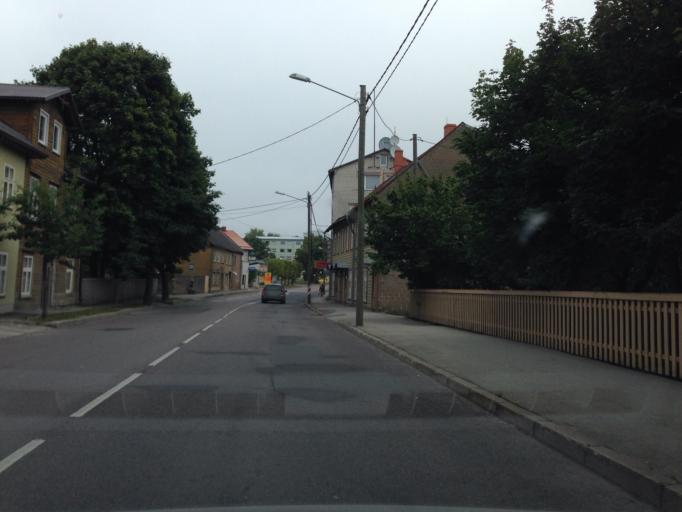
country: EE
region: Tartu
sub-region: Tartu linn
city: Tartu
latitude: 58.3701
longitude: 26.7216
